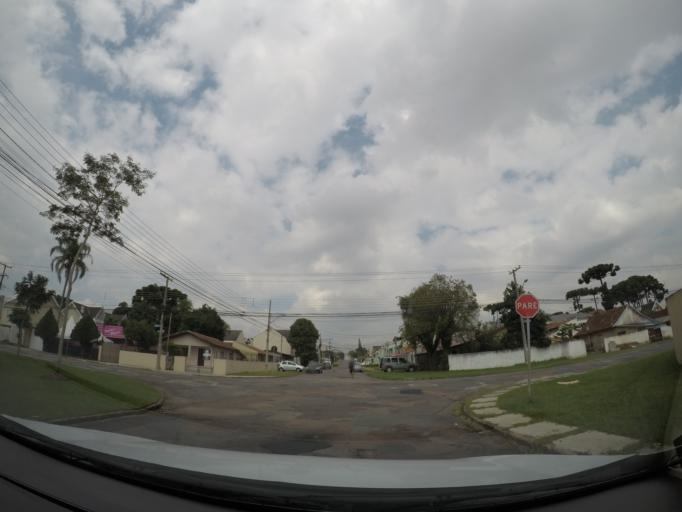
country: BR
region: Parana
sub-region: Sao Jose Dos Pinhais
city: Sao Jose dos Pinhais
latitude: -25.4956
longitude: -49.2515
